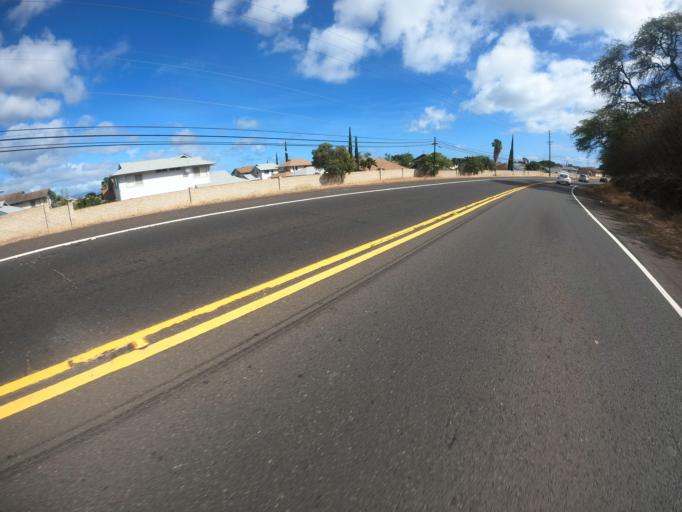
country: US
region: Hawaii
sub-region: Honolulu County
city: Makakilo City
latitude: 21.3364
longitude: -158.0729
